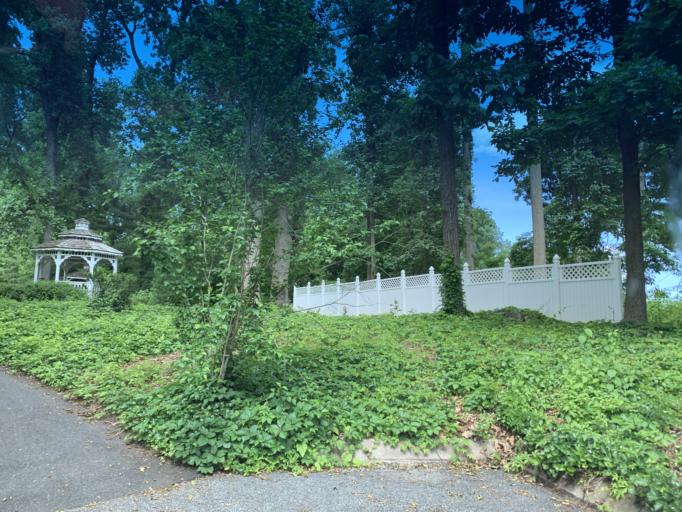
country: US
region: Maryland
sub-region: Harford County
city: Jarrettsville
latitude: 39.6247
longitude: -76.4639
